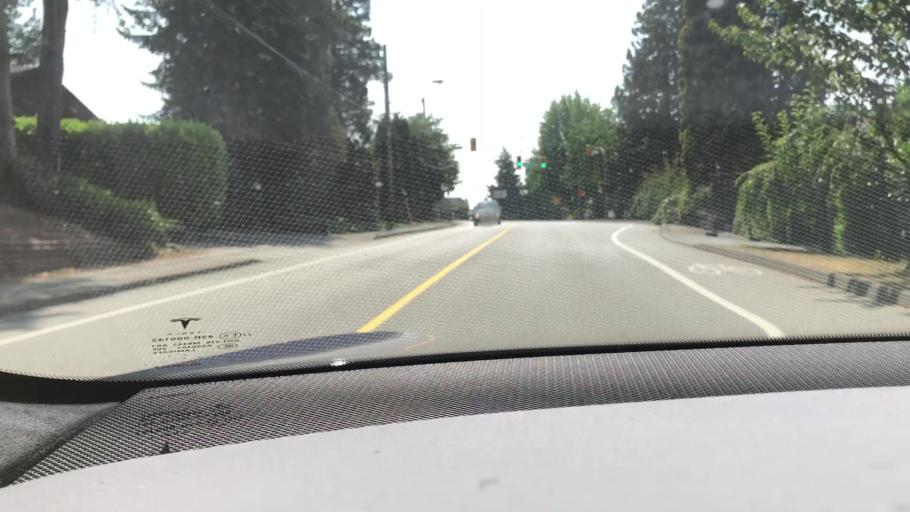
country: CA
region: British Columbia
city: Burnaby
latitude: 49.2300
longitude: -122.9650
